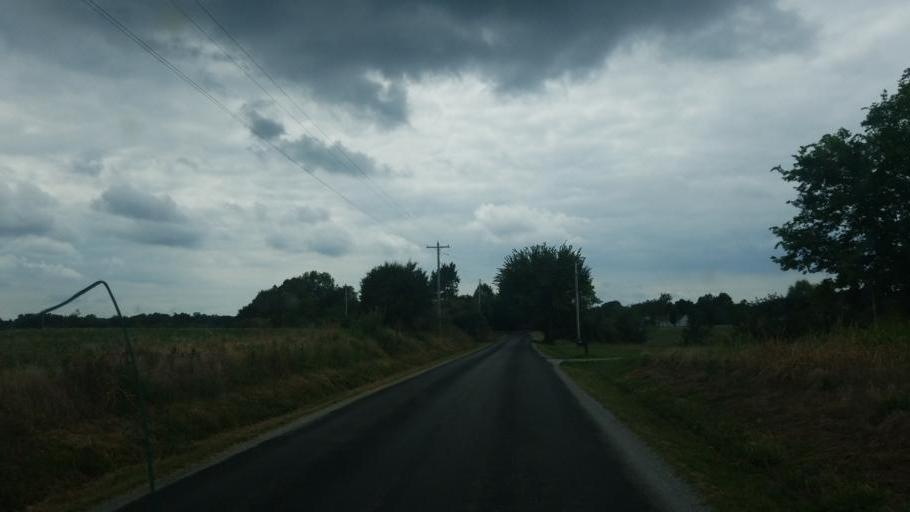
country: US
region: Illinois
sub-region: Jackson County
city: Murphysboro
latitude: 37.7093
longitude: -89.3292
